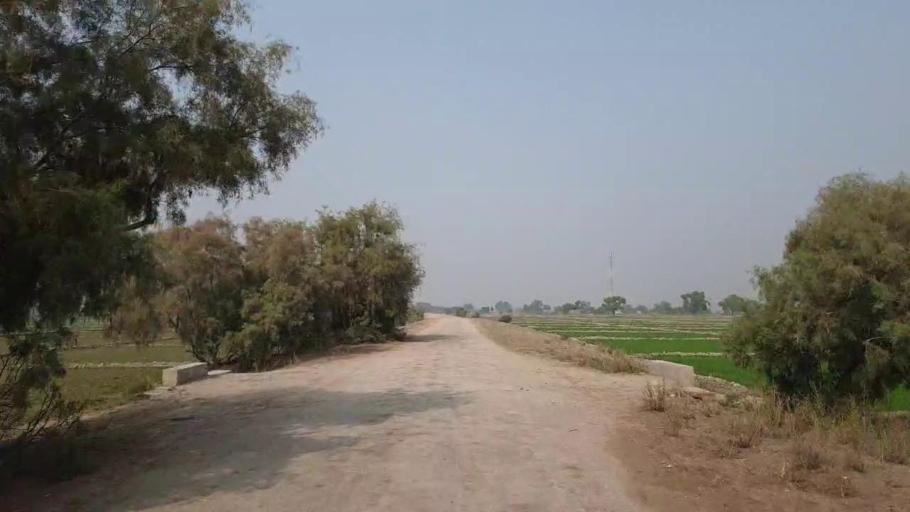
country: PK
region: Sindh
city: Bhan
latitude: 26.4937
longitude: 67.6993
